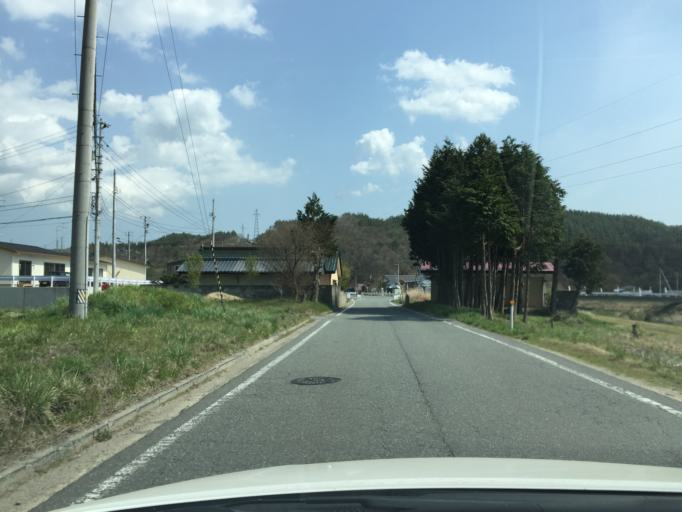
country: JP
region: Fukushima
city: Namie
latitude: 37.3300
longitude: 140.8173
